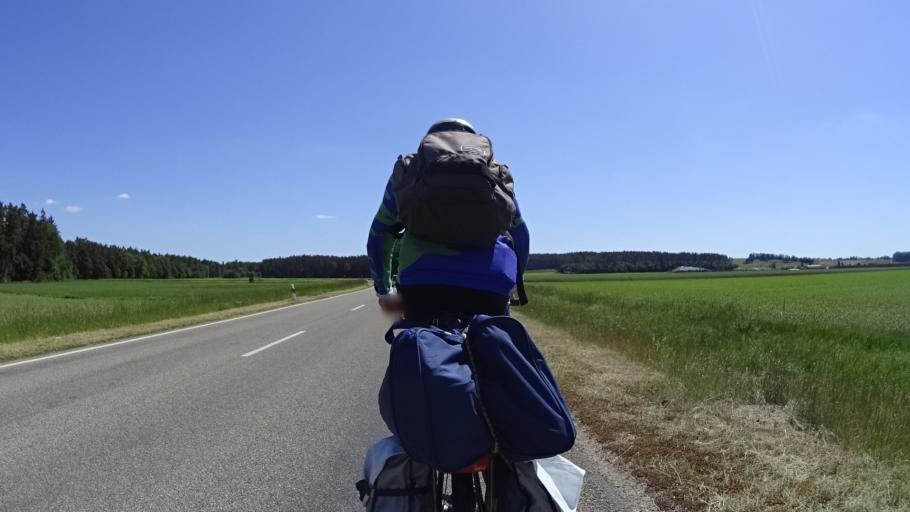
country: DE
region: Bavaria
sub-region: Regierungsbezirk Mittelfranken
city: Pfofeld
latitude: 49.1174
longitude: 10.8098
